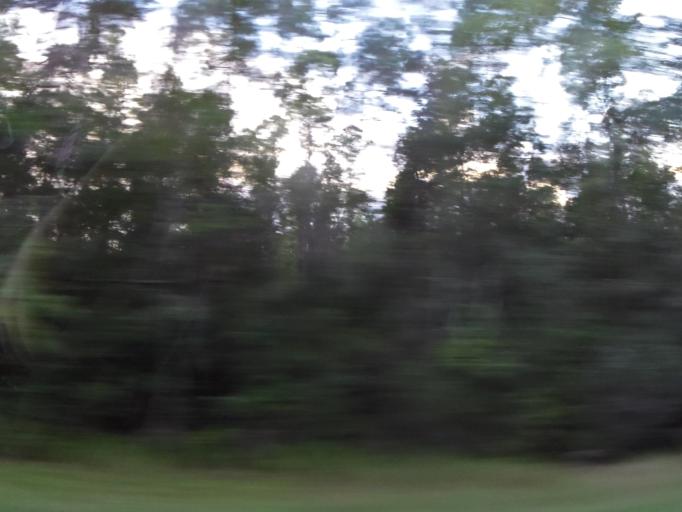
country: US
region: Georgia
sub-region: Echols County
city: Statenville
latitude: 30.7512
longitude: -83.1110
